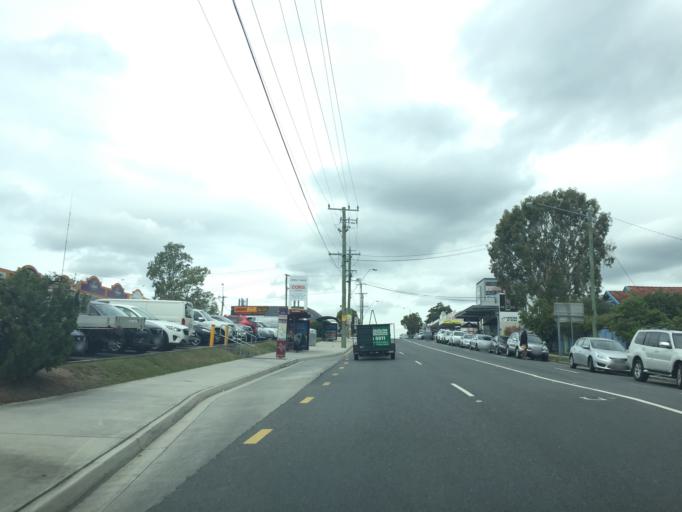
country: AU
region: Queensland
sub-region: Brisbane
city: Milton
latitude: -27.4440
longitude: 152.9913
